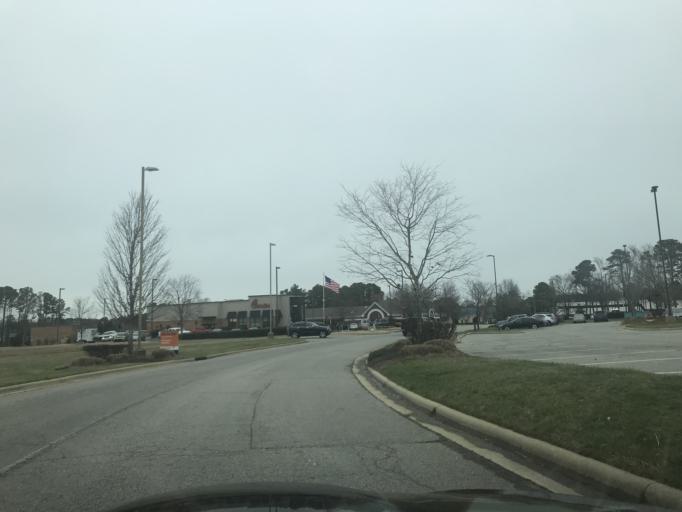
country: US
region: North Carolina
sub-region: Wake County
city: Garner
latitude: 35.7161
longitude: -78.6373
